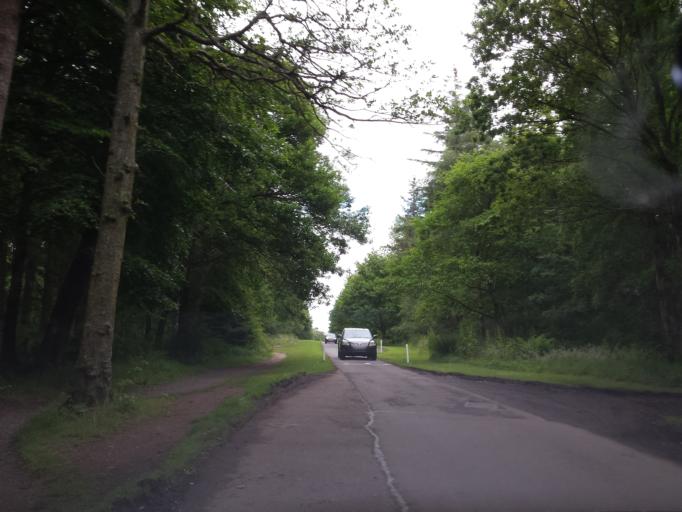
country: GB
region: Scotland
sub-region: South Ayrshire
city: Maybole
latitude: 55.3490
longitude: -4.7967
